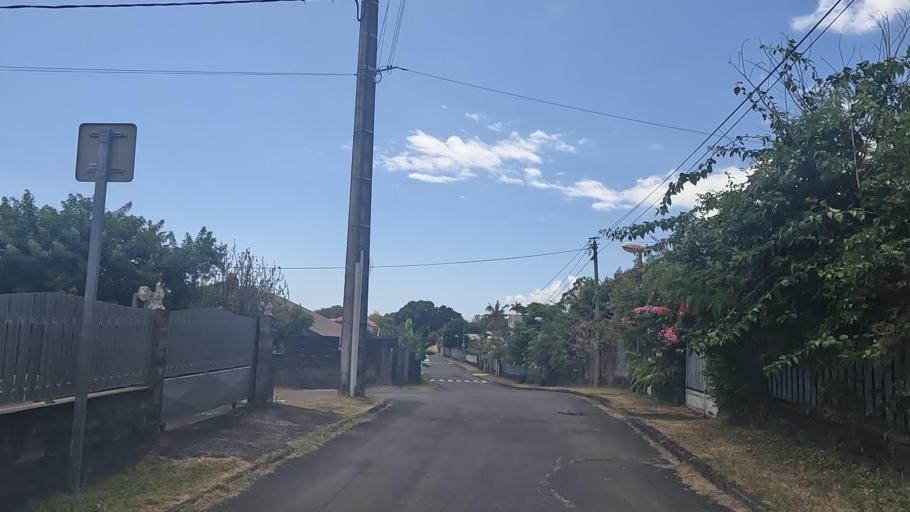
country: RE
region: Reunion
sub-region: Reunion
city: Saint-Benoit
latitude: -21.0319
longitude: 55.7037
